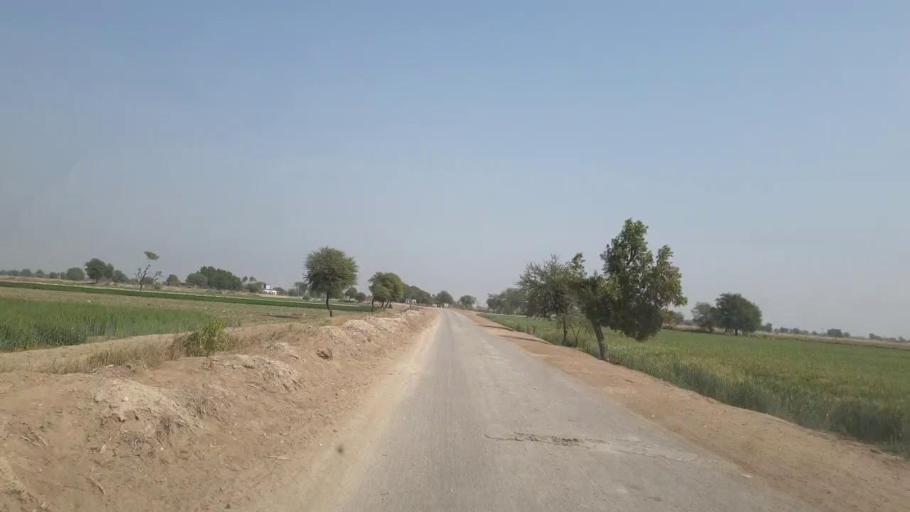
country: PK
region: Sindh
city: Mirpur Khas
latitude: 25.6464
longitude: 69.1653
